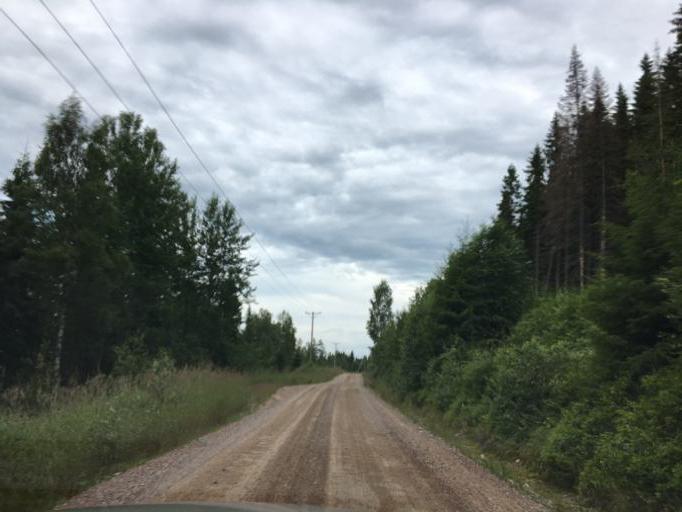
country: SE
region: Vaermland
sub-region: Filipstads Kommun
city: Lesjofors
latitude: 60.1881
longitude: 14.4000
